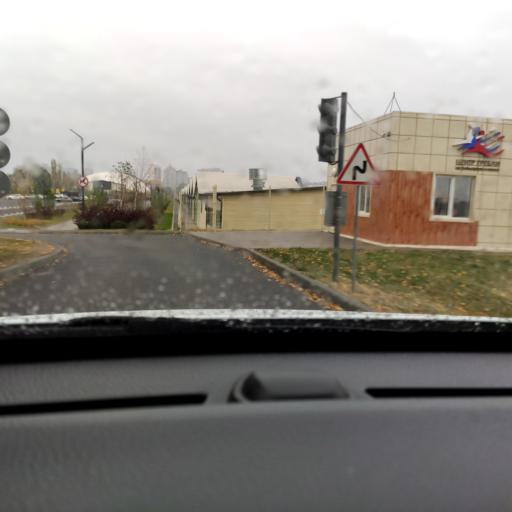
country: RU
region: Voronezj
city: Voronezh
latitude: 51.6698
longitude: 39.2301
